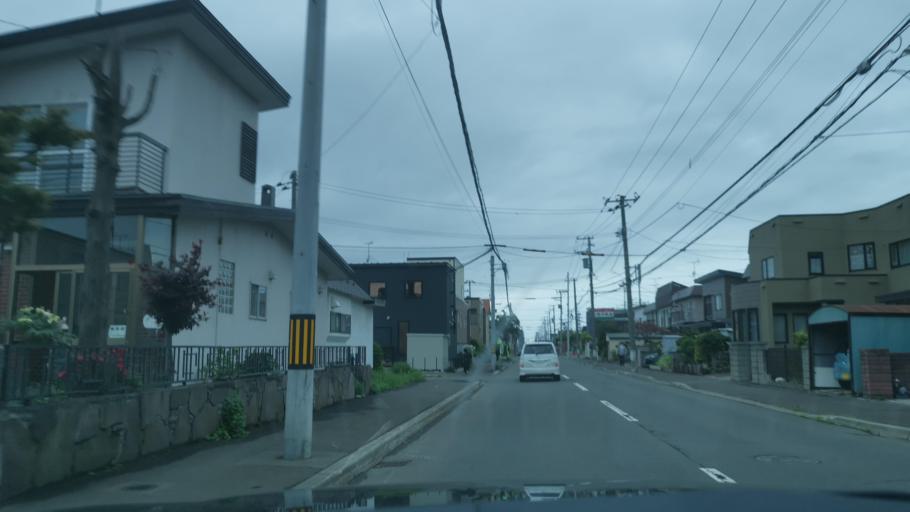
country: JP
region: Hokkaido
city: Sapporo
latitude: 43.1061
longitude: 141.3054
